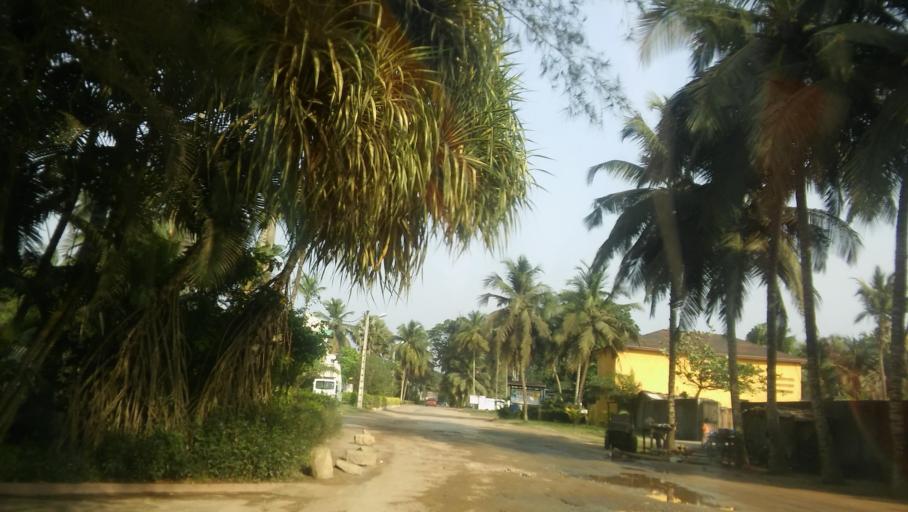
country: CI
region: Sud-Comoe
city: Grand-Bassam
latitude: 5.1963
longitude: -3.7418
